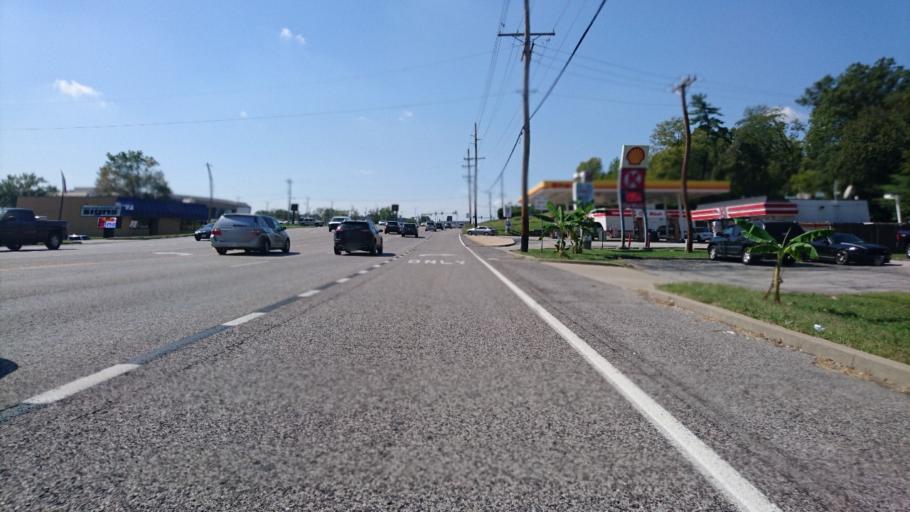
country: US
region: Missouri
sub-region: Saint Louis County
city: Town and Country
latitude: 38.5965
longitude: -90.4765
